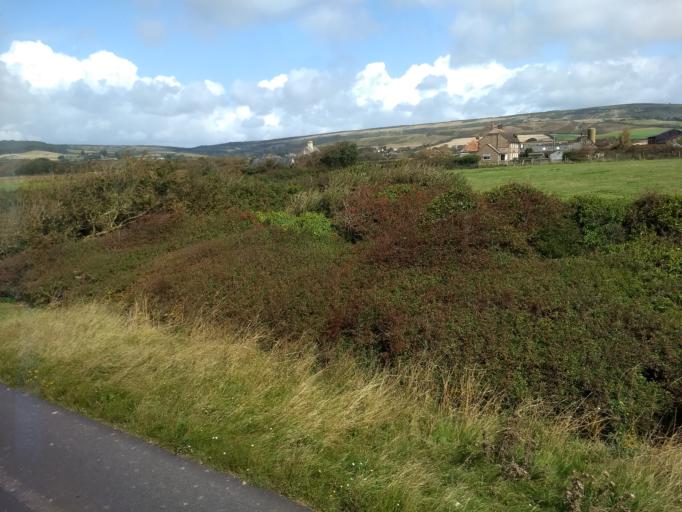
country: GB
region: England
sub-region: Isle of Wight
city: Shalfleet
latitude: 50.6341
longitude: -1.3985
